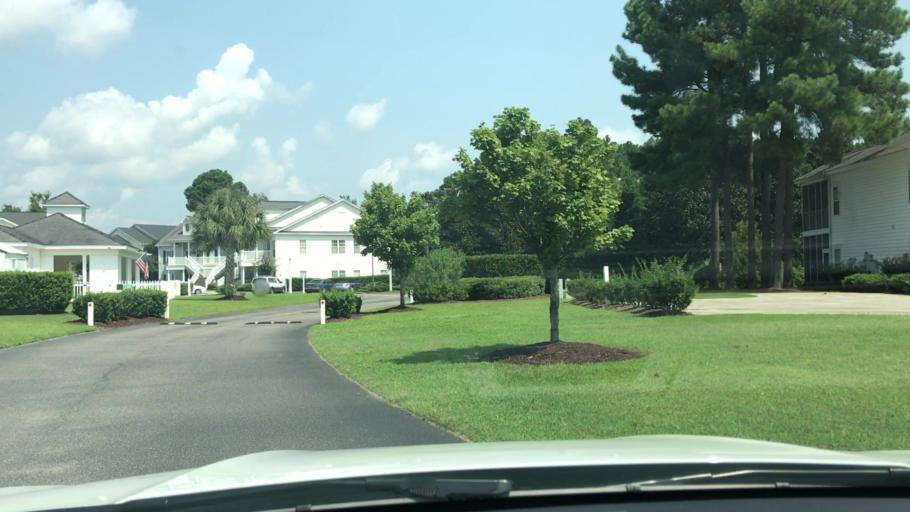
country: US
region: South Carolina
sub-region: Horry County
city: Forestbrook
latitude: 33.7779
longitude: -78.9650
